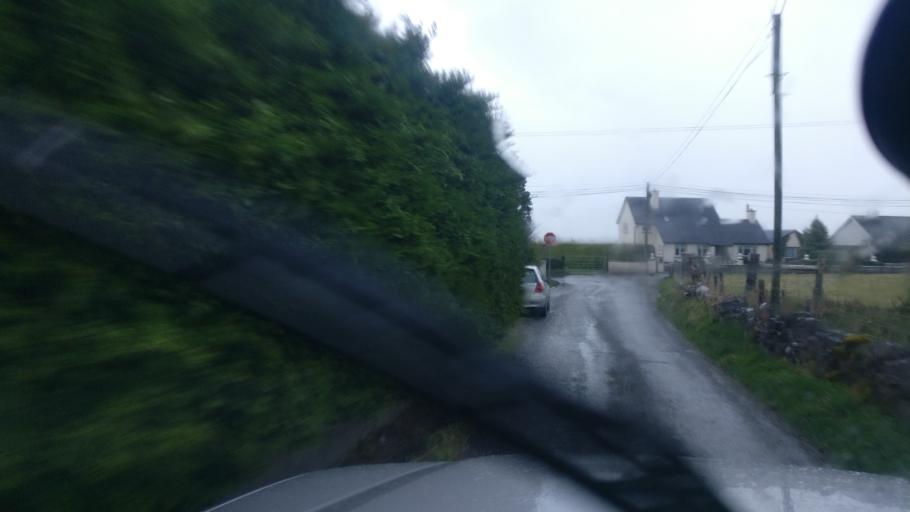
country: IE
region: Connaught
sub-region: County Galway
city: Loughrea
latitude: 53.2281
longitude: -8.4273
